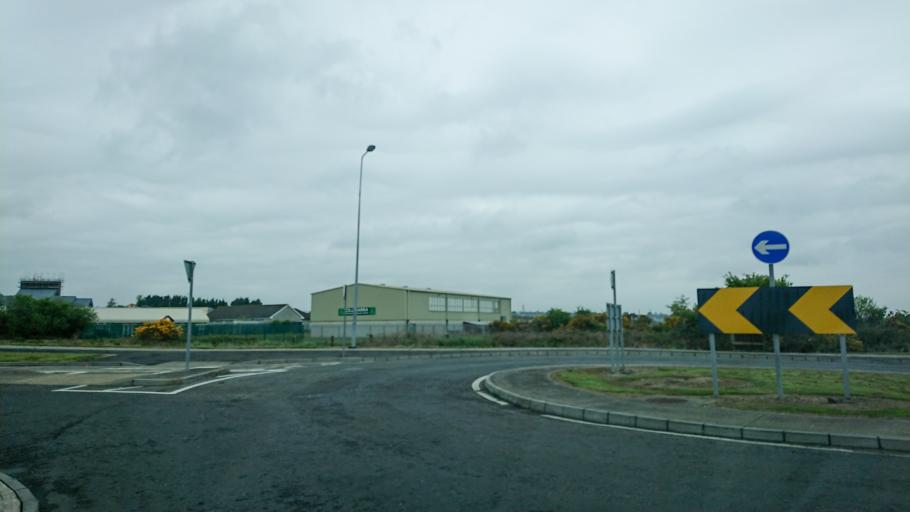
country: IE
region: Munster
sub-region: Waterford
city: Waterford
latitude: 52.2378
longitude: -7.1419
